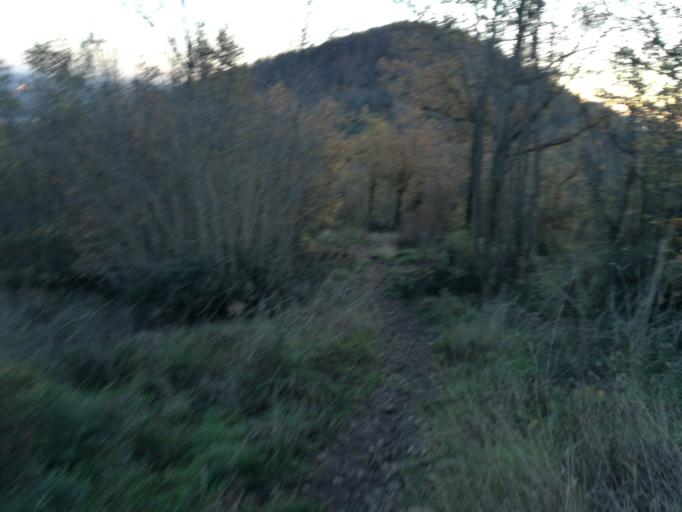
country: IT
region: Veneto
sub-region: Provincia di Padova
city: Battaglia Terme
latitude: 45.3041
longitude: 11.7683
